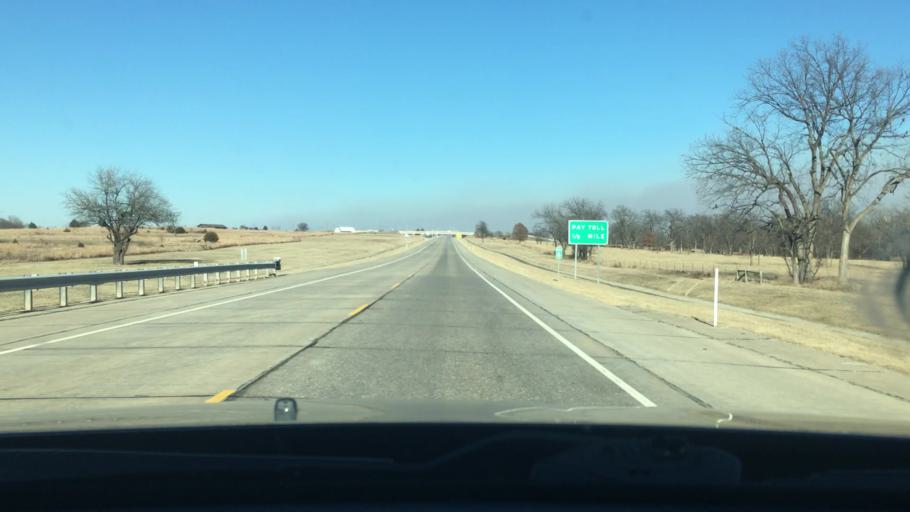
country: US
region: Oklahoma
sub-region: Murray County
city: Sulphur
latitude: 34.5572
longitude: -96.9385
